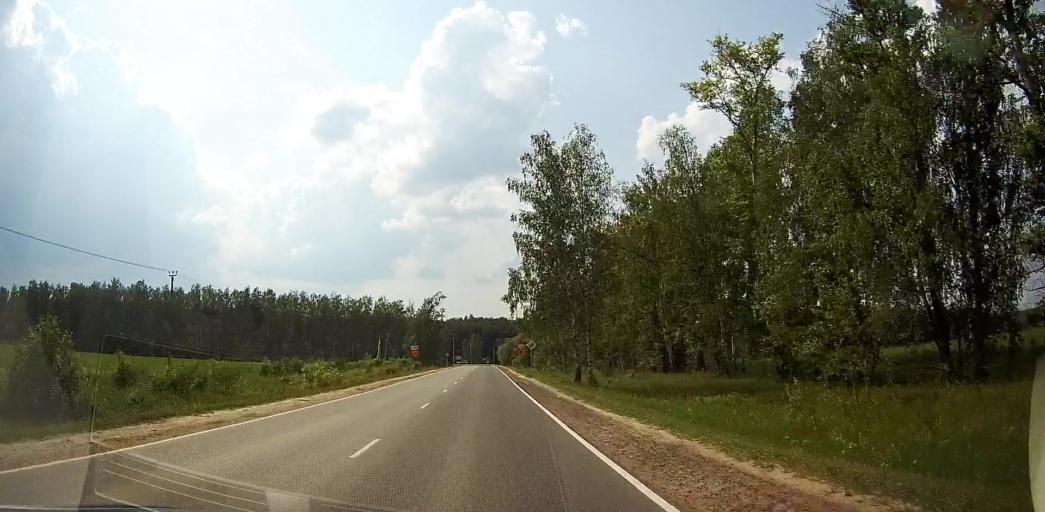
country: RU
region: Moskovskaya
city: Zhilevo
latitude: 55.0578
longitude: 37.9589
